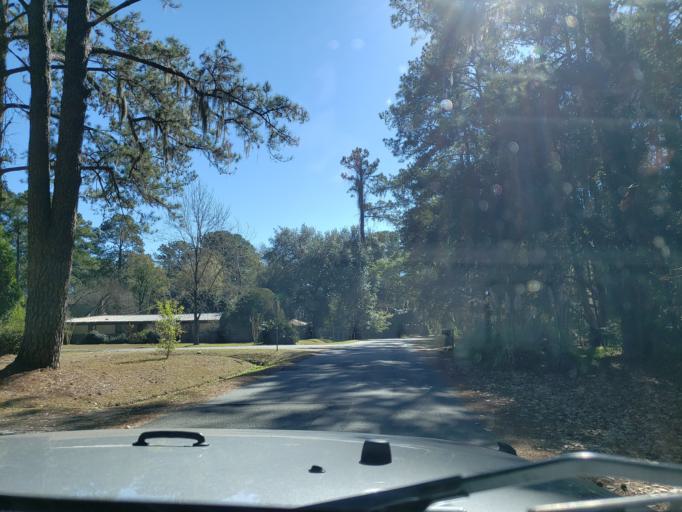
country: US
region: Georgia
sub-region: Chatham County
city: Wilmington Island
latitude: 32.0375
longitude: -80.9756
